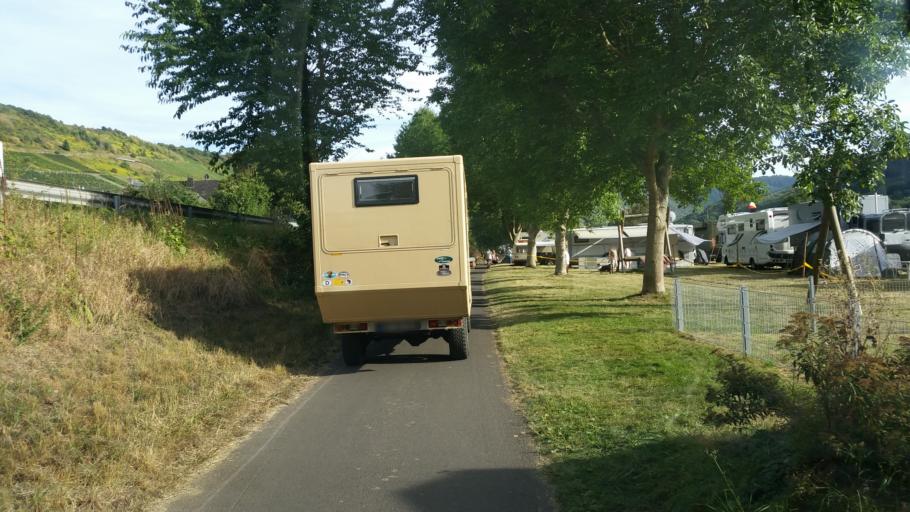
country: DE
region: Rheinland-Pfalz
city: Enkirch
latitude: 49.9822
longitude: 7.1233
